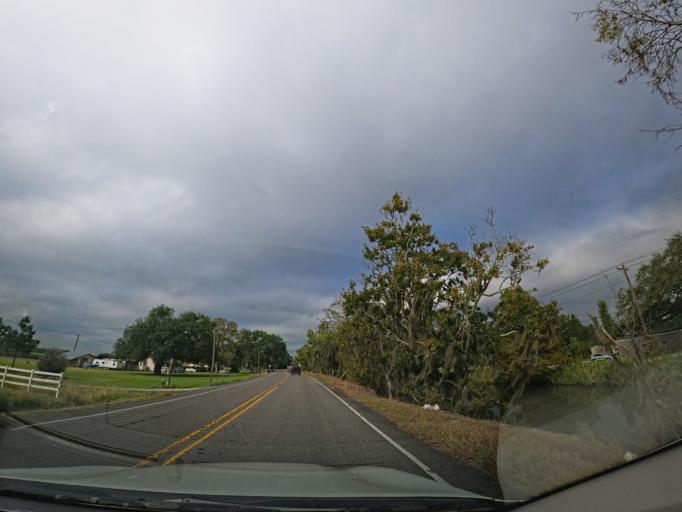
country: US
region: Louisiana
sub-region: Terrebonne Parish
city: Bayou Cane
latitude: 29.6090
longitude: -90.8514
